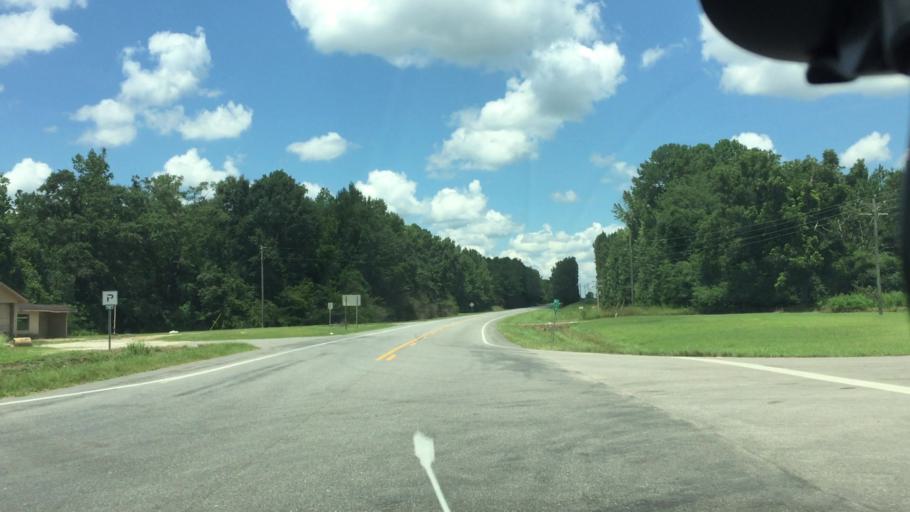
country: US
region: Alabama
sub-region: Coffee County
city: New Brockton
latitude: 31.4892
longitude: -85.9137
